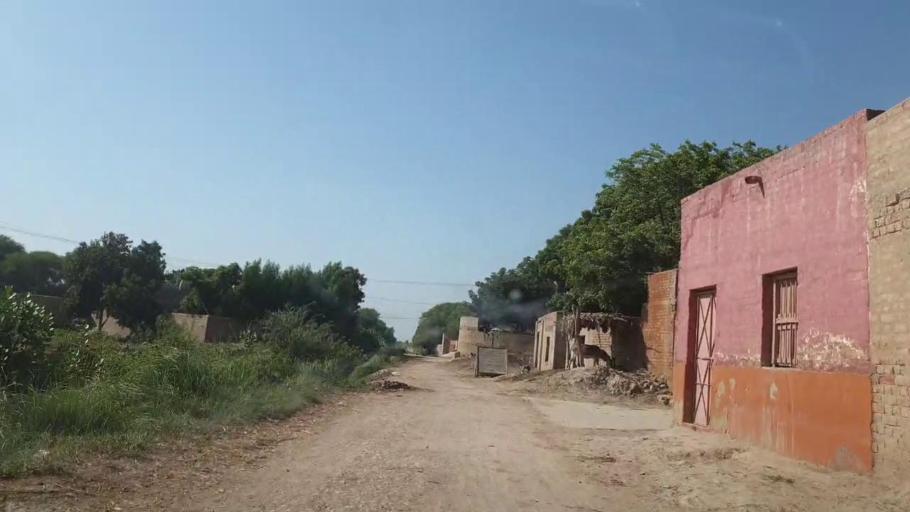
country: PK
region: Sindh
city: Tando Jam
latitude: 25.3138
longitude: 68.6080
